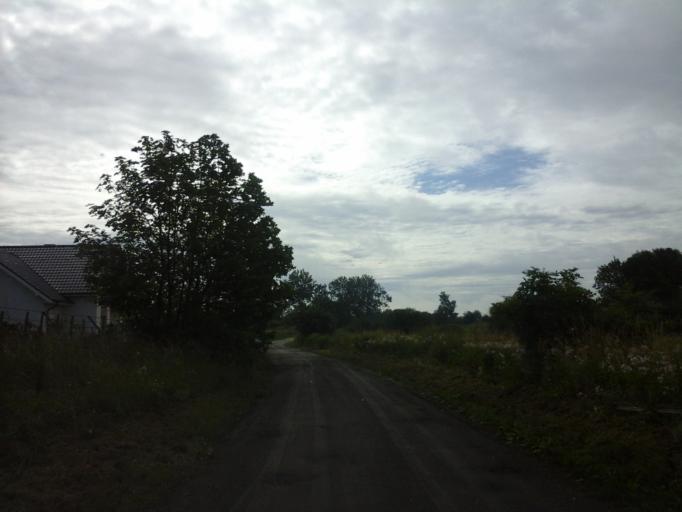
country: PL
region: West Pomeranian Voivodeship
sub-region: Powiat choszczenski
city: Choszczno
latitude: 53.1555
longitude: 15.4172
